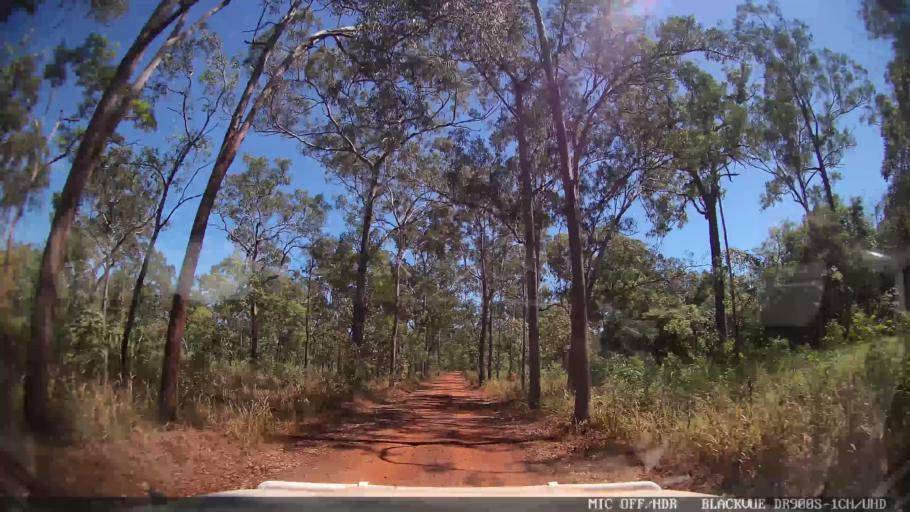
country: AU
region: Queensland
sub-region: Torres
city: Thursday Island
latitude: -10.9183
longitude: 142.2563
